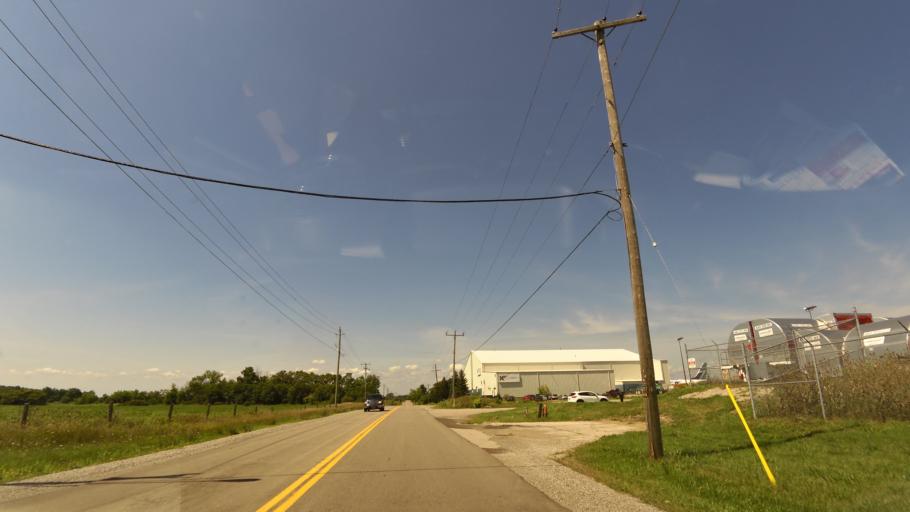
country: CA
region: Ontario
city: Ancaster
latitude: 43.1605
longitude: -79.9325
